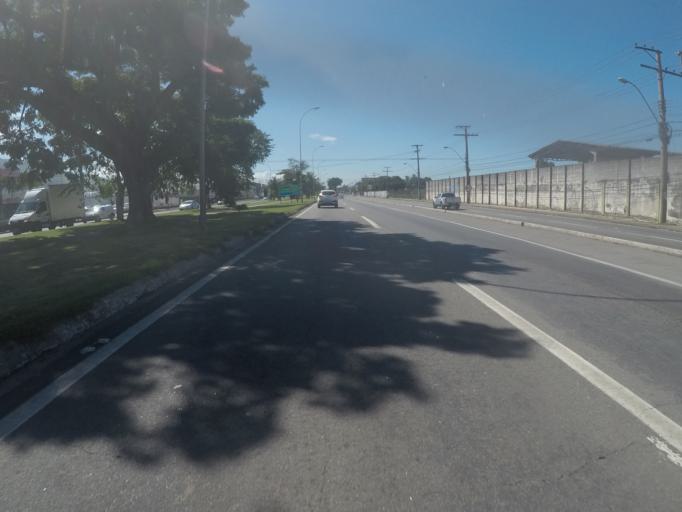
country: BR
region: Espirito Santo
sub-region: Serra
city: Serra
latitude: -20.2123
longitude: -40.2696
